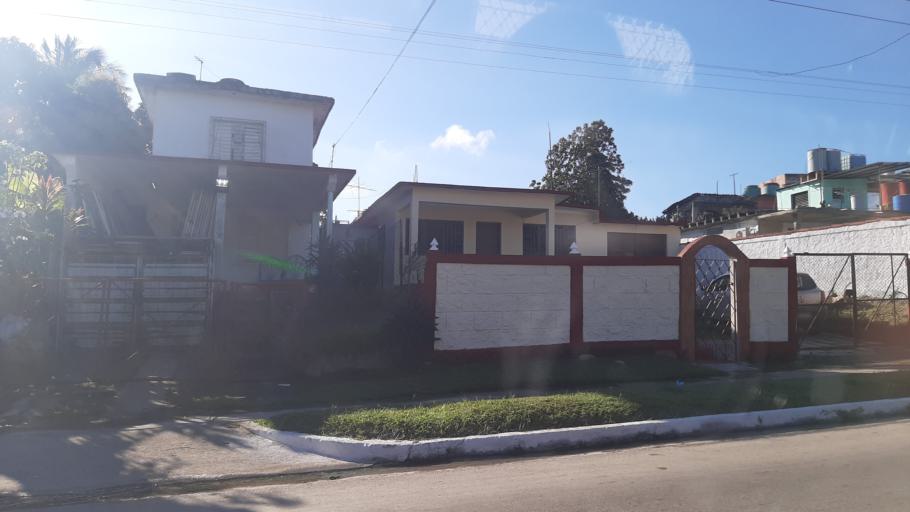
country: CU
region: Villa Clara
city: Santa Clara
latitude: 22.4146
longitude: -79.9492
